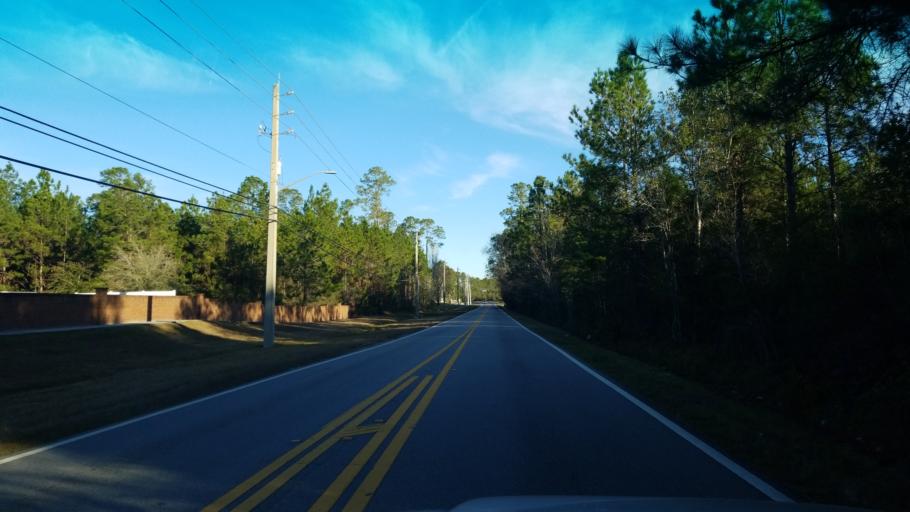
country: US
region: Florida
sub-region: Duval County
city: Baldwin
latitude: 30.3294
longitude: -81.8486
